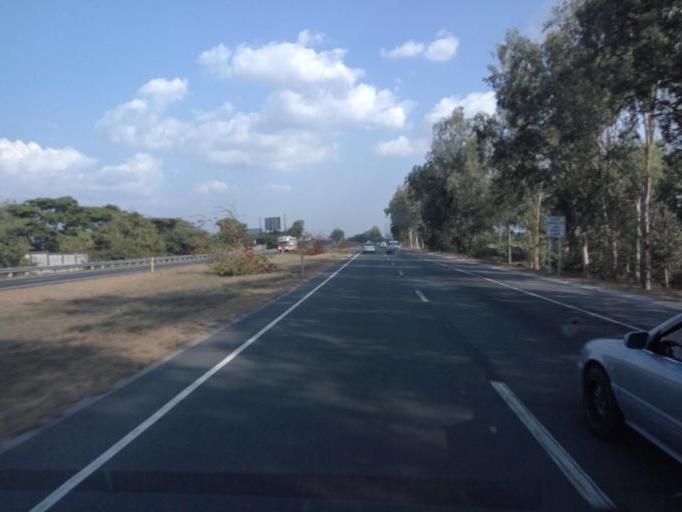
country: PH
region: Central Luzon
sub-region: Province of Pampanga
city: Balibago
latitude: 15.1523
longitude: 120.6214
